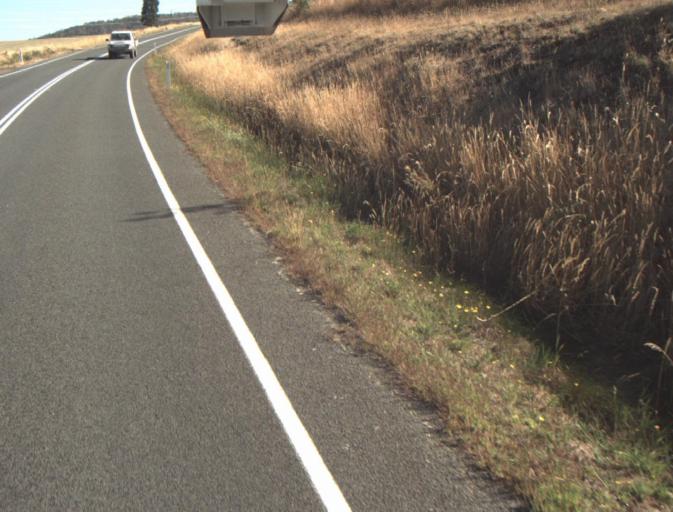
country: AU
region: Tasmania
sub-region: Launceston
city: Newstead
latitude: -41.4148
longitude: 147.2805
